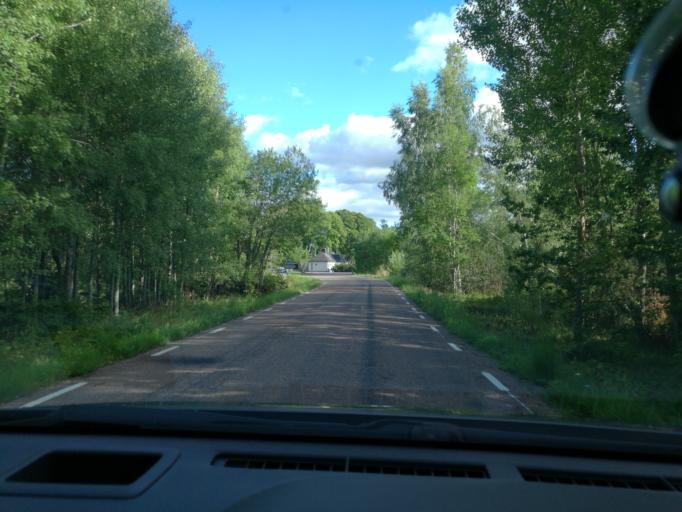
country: SE
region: Vaestmanland
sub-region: Hallstahammars Kommun
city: Kolback
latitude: 59.5388
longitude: 16.1346
